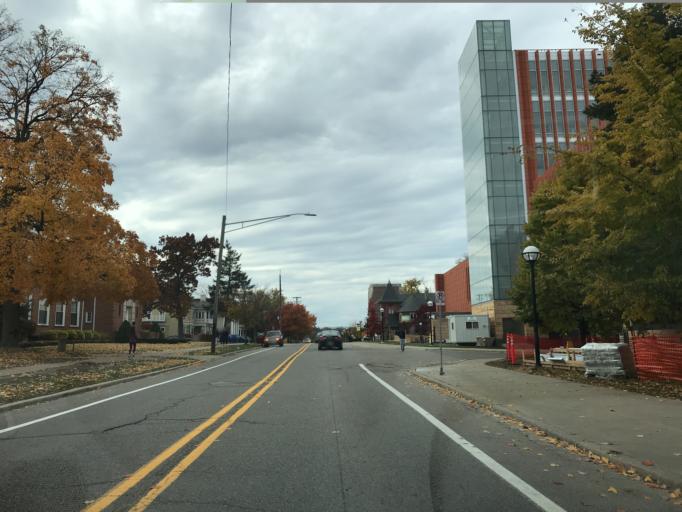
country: US
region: Michigan
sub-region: Washtenaw County
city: Ann Arbor
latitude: 42.2720
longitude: -83.7367
